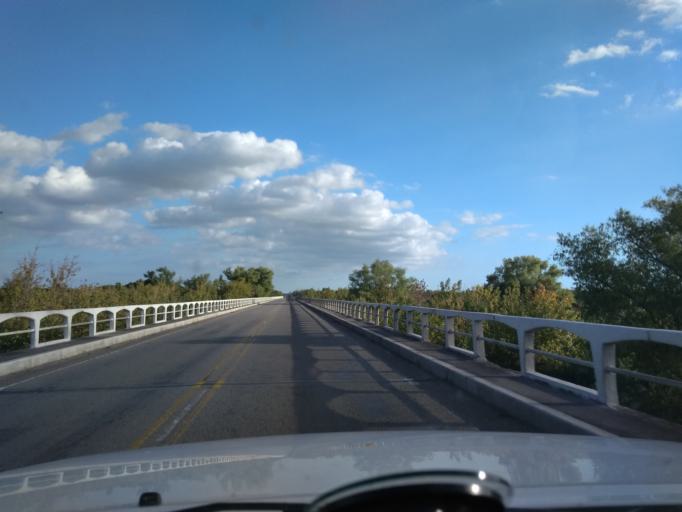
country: UY
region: Florida
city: Cardal
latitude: -34.3593
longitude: -56.2490
